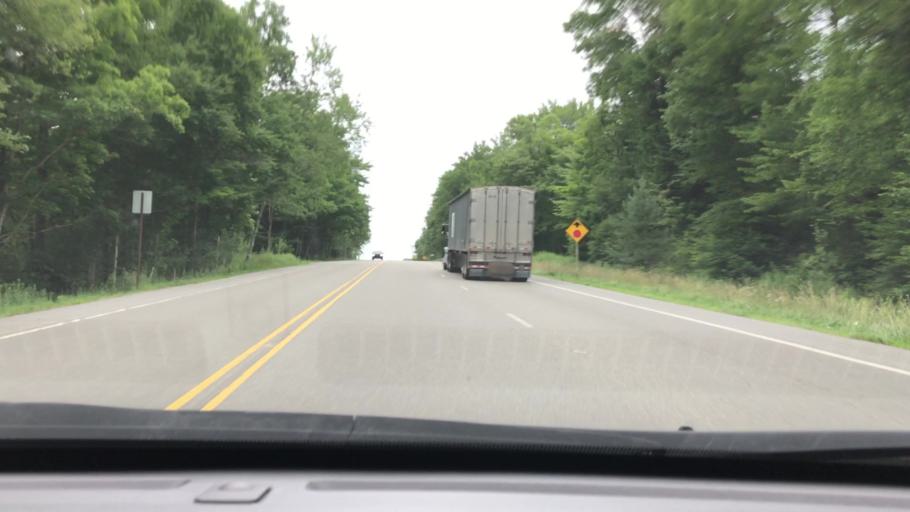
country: US
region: Pennsylvania
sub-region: McKean County
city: Kane
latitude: 41.7034
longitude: -78.6927
